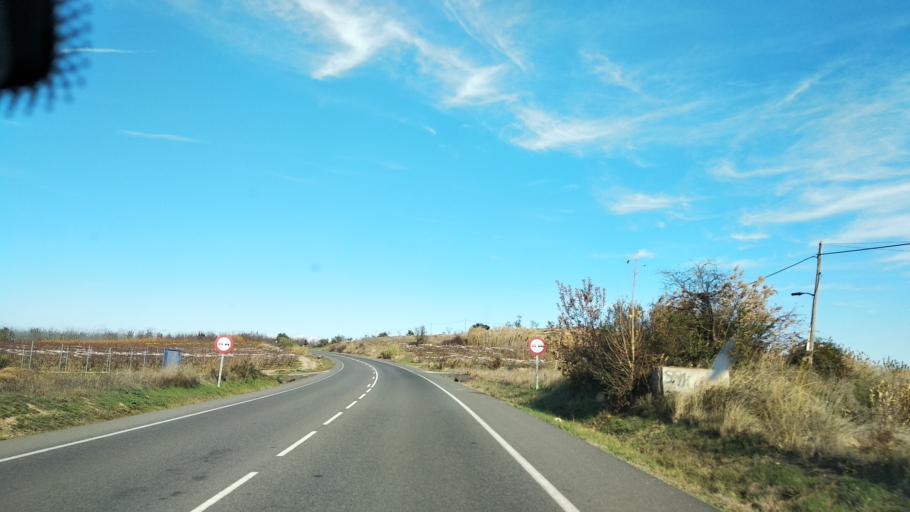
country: ES
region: Catalonia
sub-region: Provincia de Lleida
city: Alcoletge
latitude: 41.6675
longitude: 0.6672
